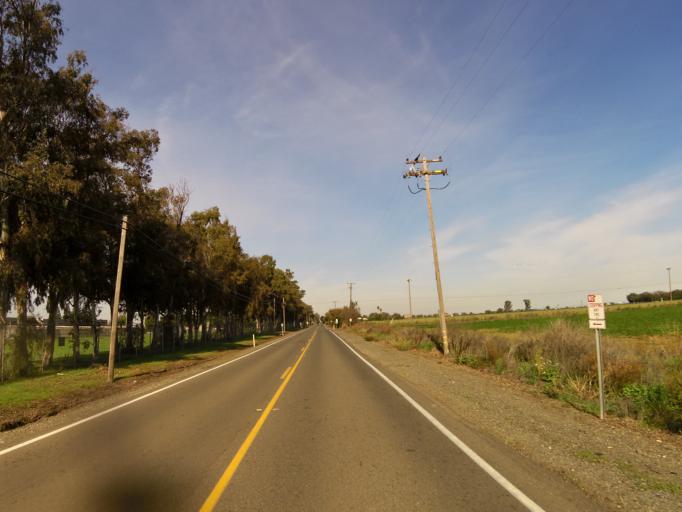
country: US
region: California
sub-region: San Joaquin County
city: Thornton
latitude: 38.3039
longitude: -121.4200
